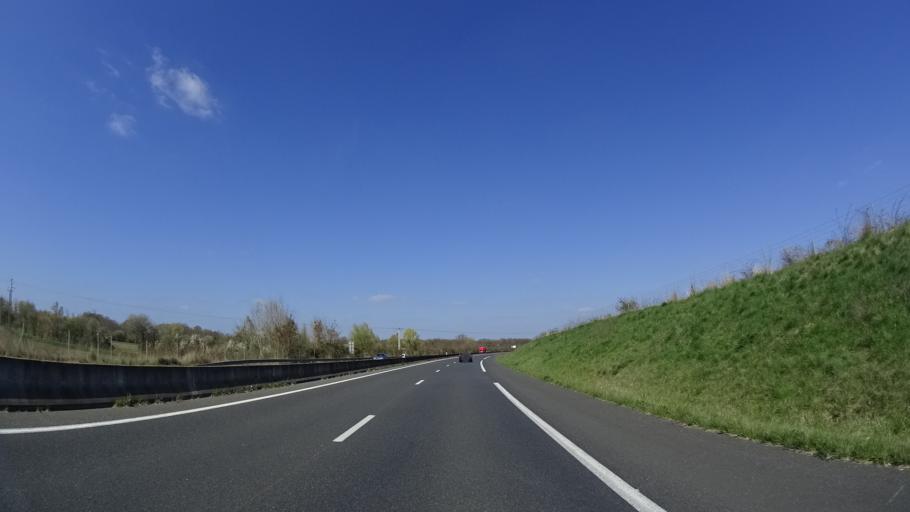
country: FR
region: Pays de la Loire
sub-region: Departement de Maine-et-Loire
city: Saint-Jean
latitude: 47.2940
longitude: -0.3881
